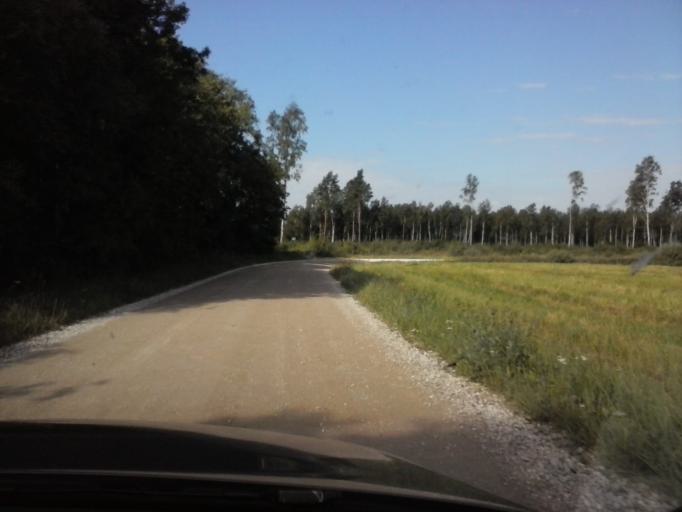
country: EE
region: Laeaene
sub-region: Ridala Parish
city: Uuemoisa
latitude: 58.8812
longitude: 23.5861
